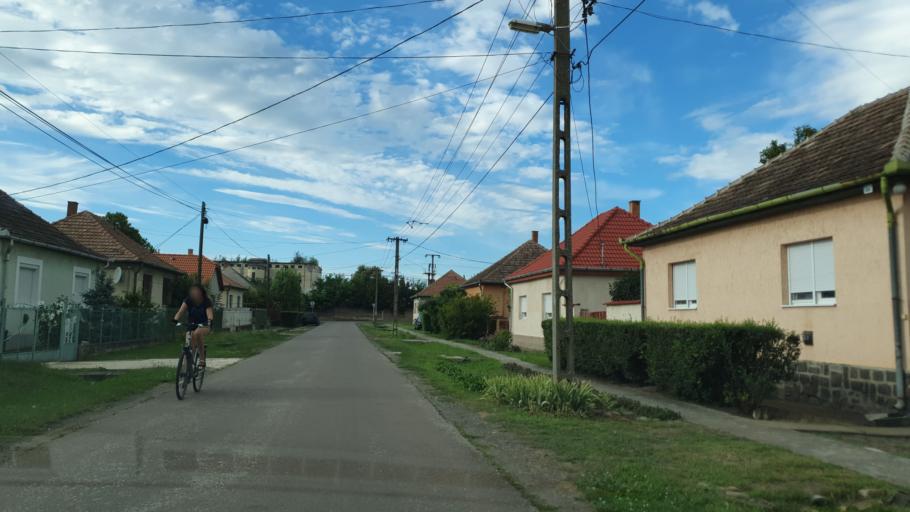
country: HU
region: Heves
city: Zagyvaszanto
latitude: 47.7617
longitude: 19.6775
